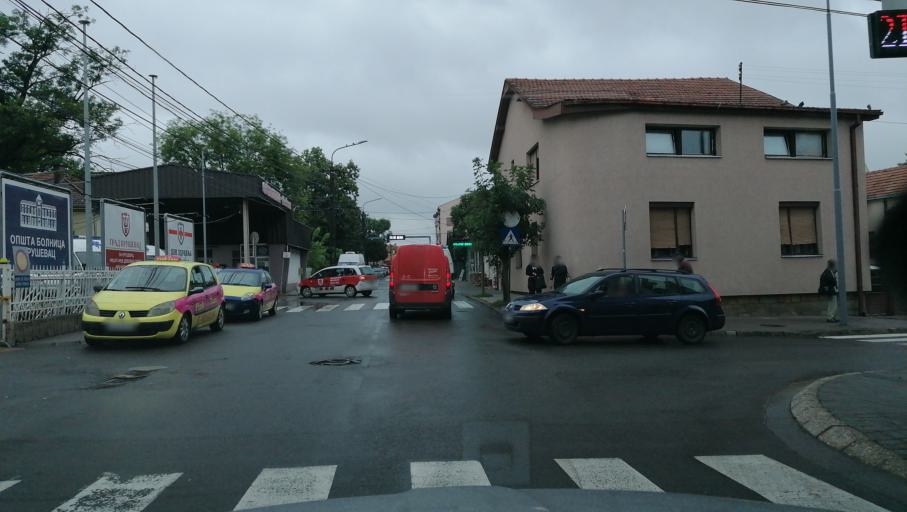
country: RS
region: Central Serbia
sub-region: Rasinski Okrug
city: Krusevac
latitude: 43.5813
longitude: 21.3217
